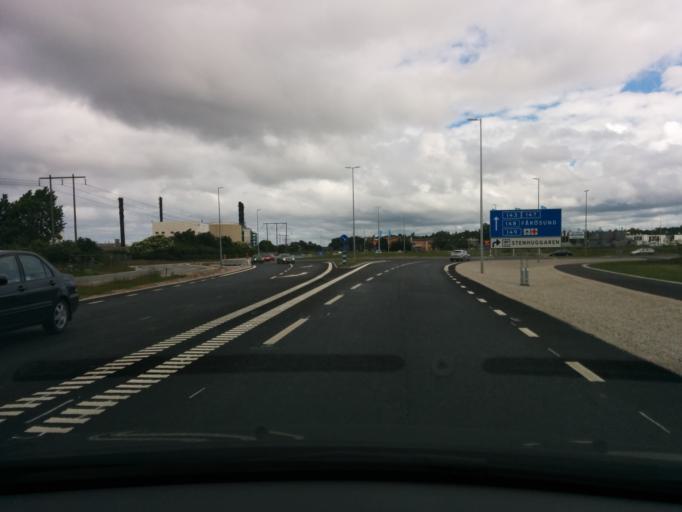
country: SE
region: Gotland
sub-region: Gotland
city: Visby
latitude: 57.6202
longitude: 18.3179
